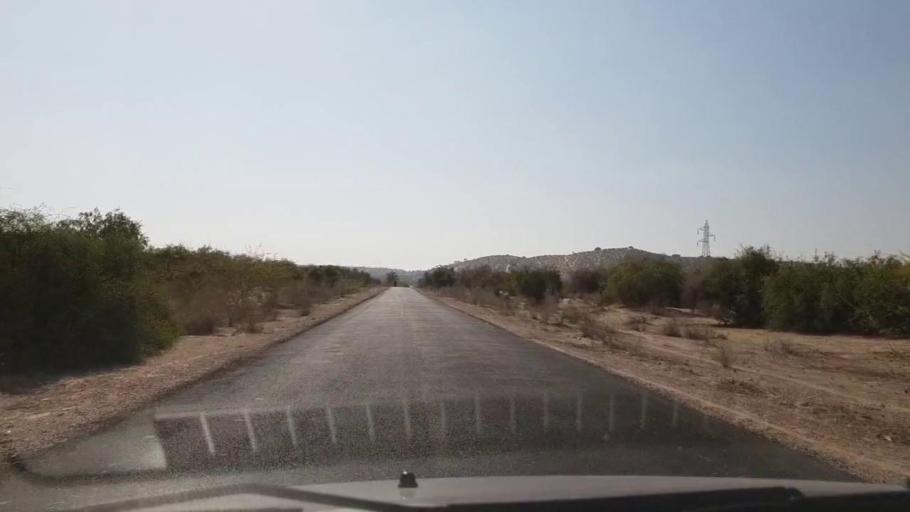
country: PK
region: Sindh
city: Mithi
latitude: 24.6483
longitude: 69.7495
